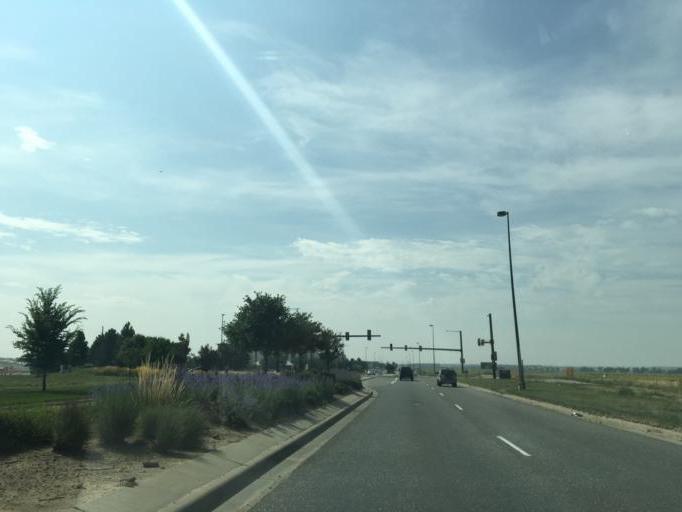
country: US
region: Colorado
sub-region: Adams County
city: Aurora
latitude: 39.8142
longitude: -104.7722
